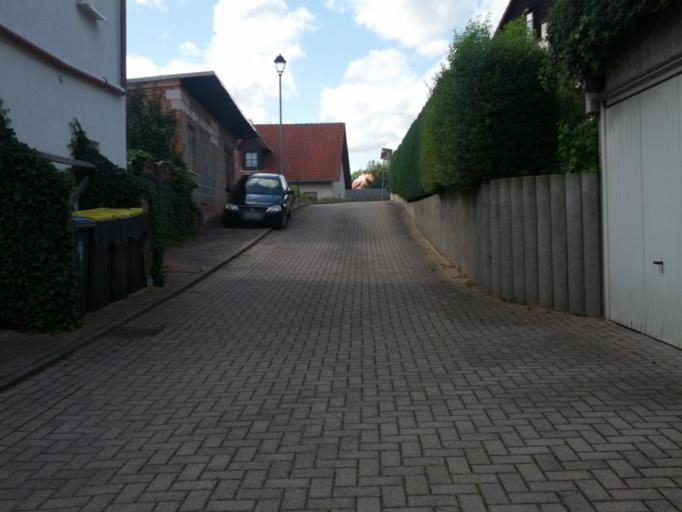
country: DE
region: Thuringia
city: Krauthausen
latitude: 50.9926
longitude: 10.2575
